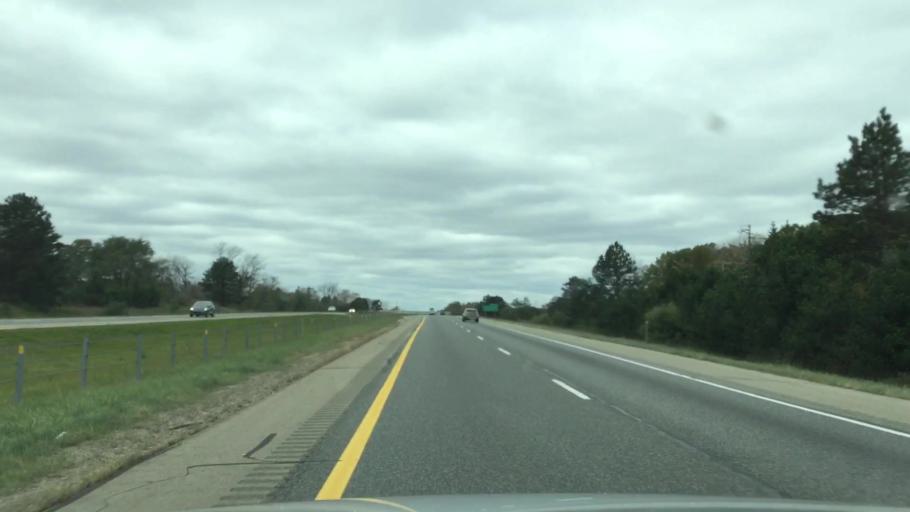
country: US
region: Michigan
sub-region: Washtenaw County
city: Chelsea
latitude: 42.2987
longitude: -83.9639
